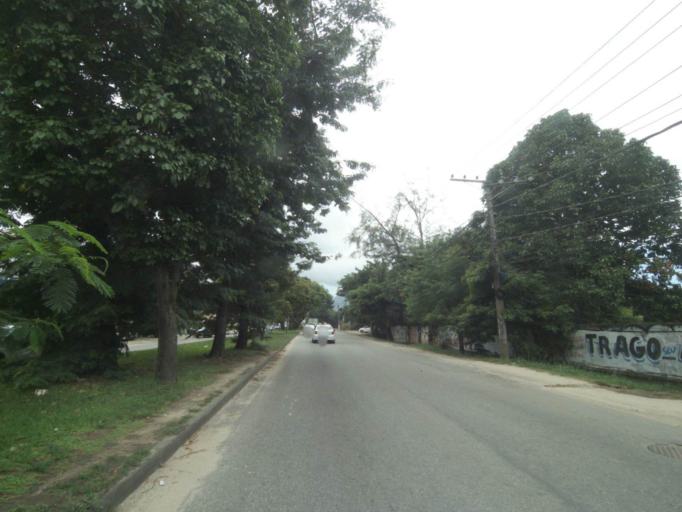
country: BR
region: Rio de Janeiro
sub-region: Nilopolis
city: Nilopolis
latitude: -22.9616
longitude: -43.3962
